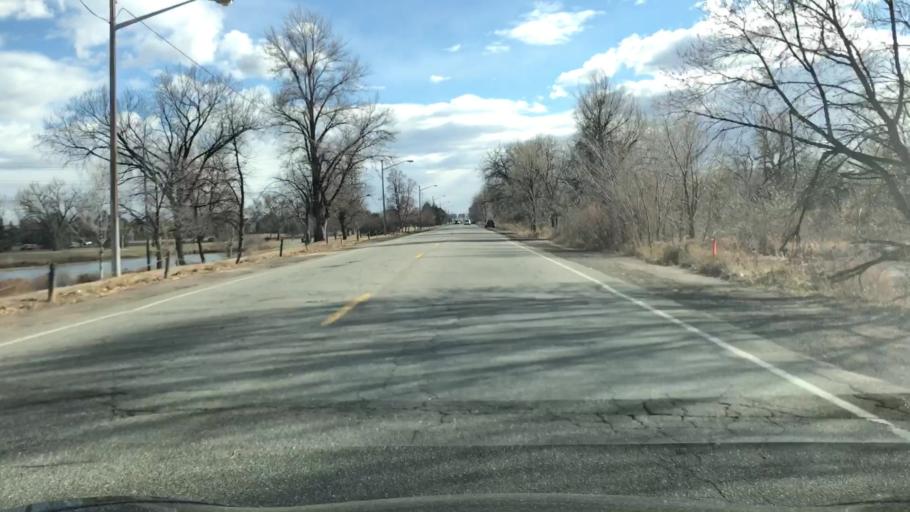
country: US
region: Colorado
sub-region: Arapahoe County
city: Glendale
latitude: 39.6959
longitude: -104.9208
